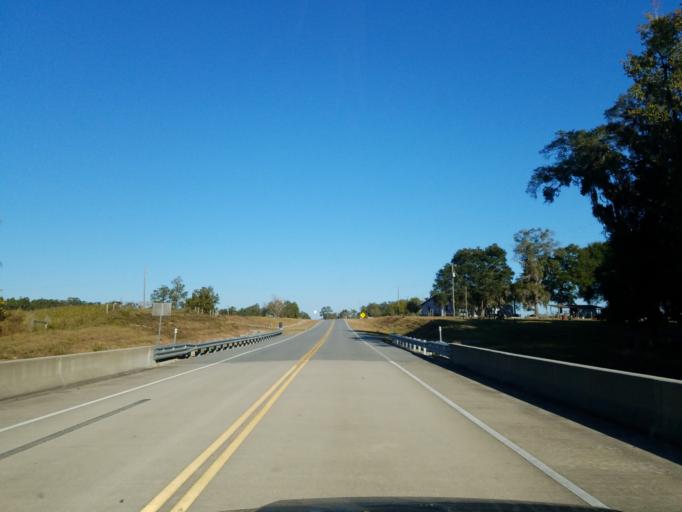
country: US
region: Georgia
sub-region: Echols County
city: Statenville
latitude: 30.6288
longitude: -83.0880
